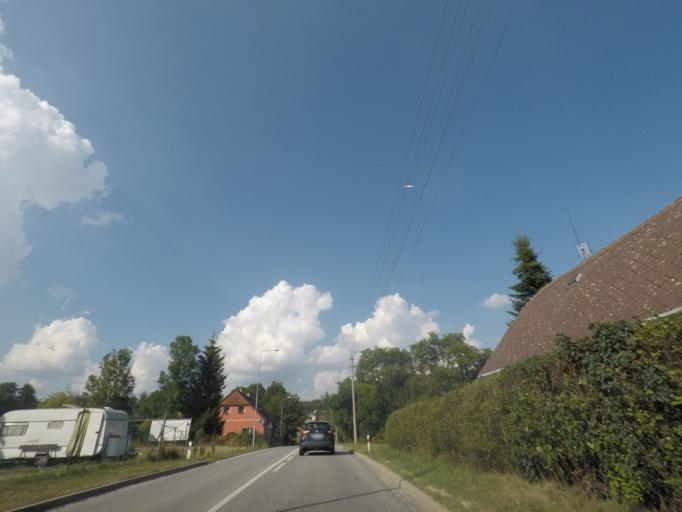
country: CZ
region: Kralovehradecky
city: Dvur Kralove nad Labem
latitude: 50.4575
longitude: 15.8590
